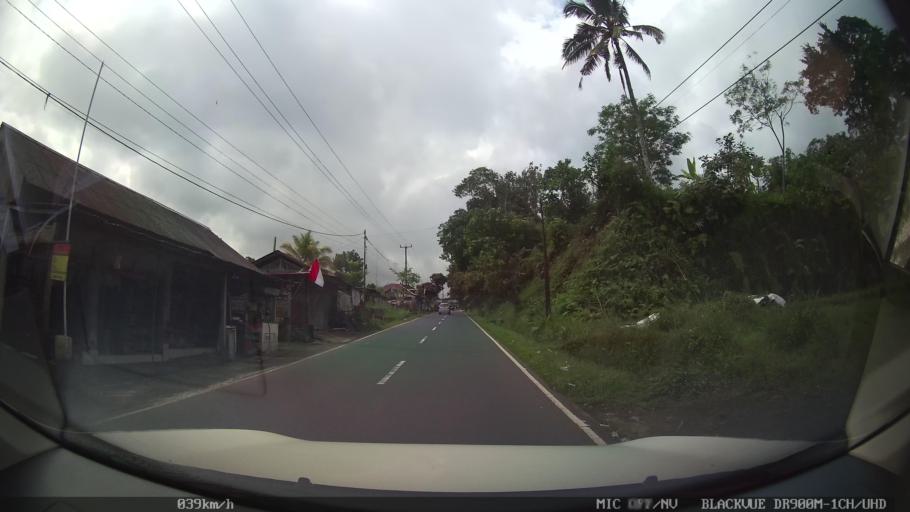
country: ID
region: Bali
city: Petang
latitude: -8.3762
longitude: 115.2237
